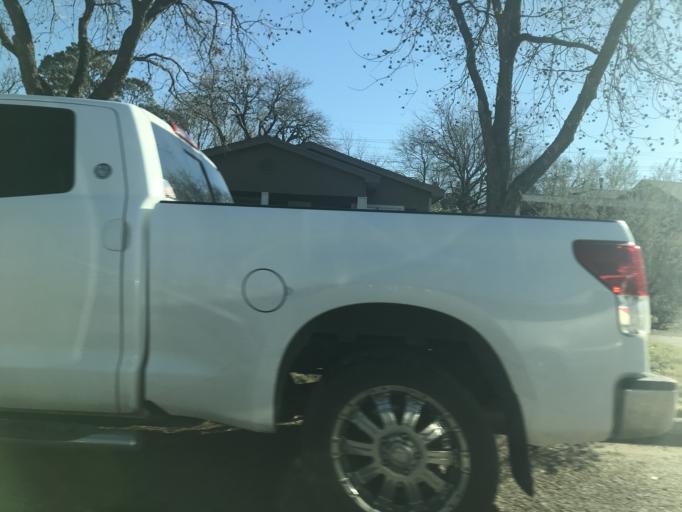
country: US
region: Texas
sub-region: Taylor County
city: Abilene
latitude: 32.4363
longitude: -99.7537
